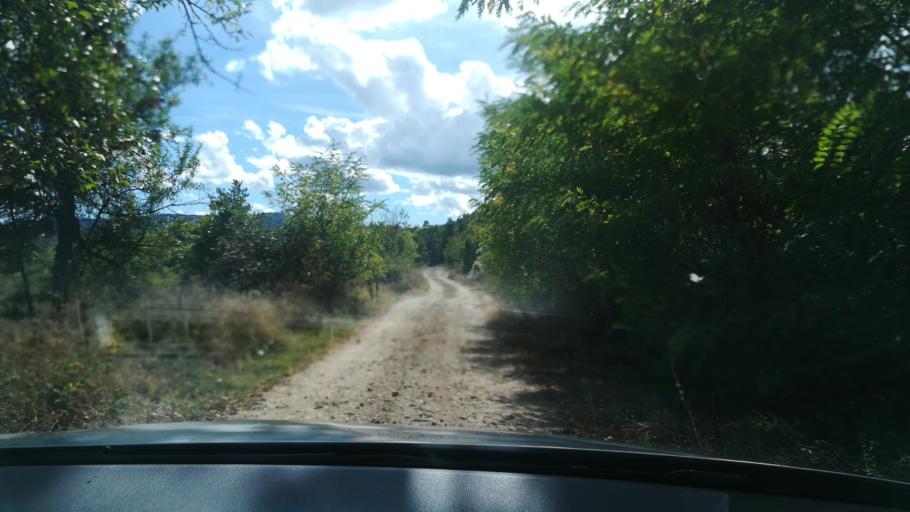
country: MK
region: Delcevo
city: Delcevo
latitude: 41.9010
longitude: 22.8057
